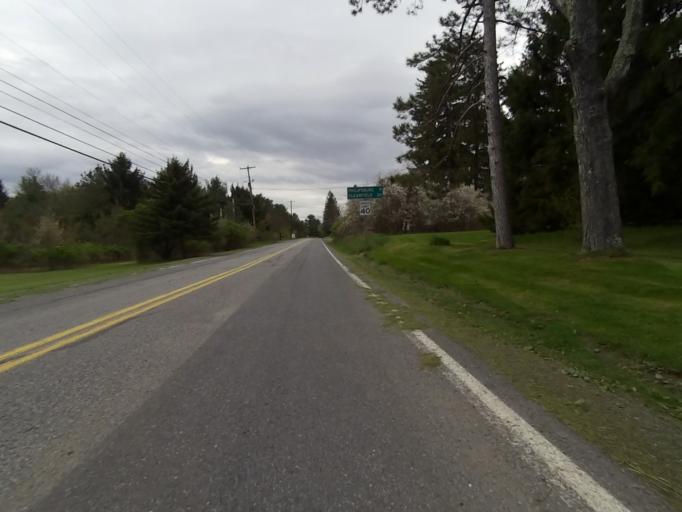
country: US
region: Pennsylvania
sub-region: Centre County
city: Stormstown
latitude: 40.9137
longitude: -78.0687
